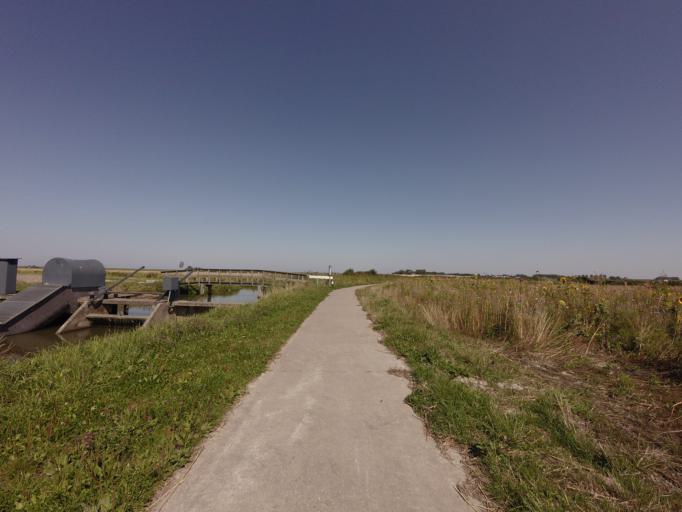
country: NL
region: Friesland
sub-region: Gemeente Dongeradeel
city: Anjum
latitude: 53.3916
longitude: 6.0668
